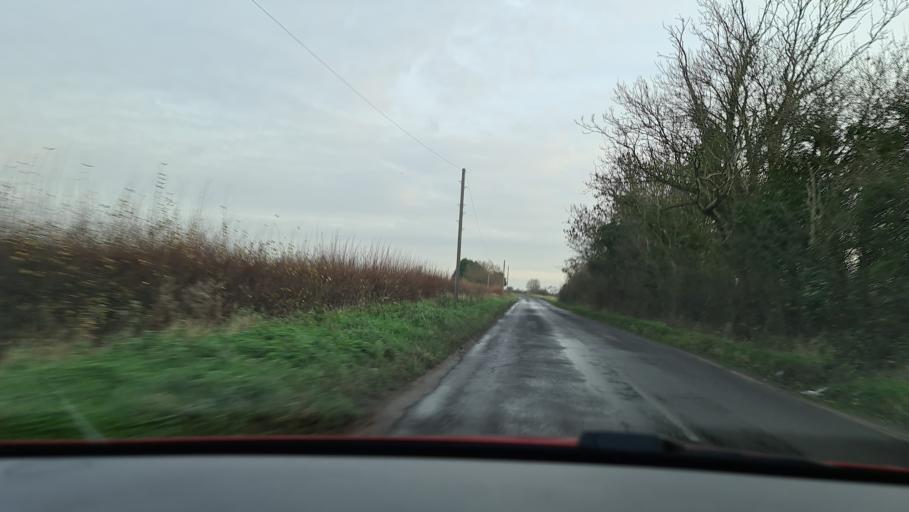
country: GB
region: England
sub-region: Oxfordshire
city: Bicester
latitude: 51.8338
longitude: -1.2050
